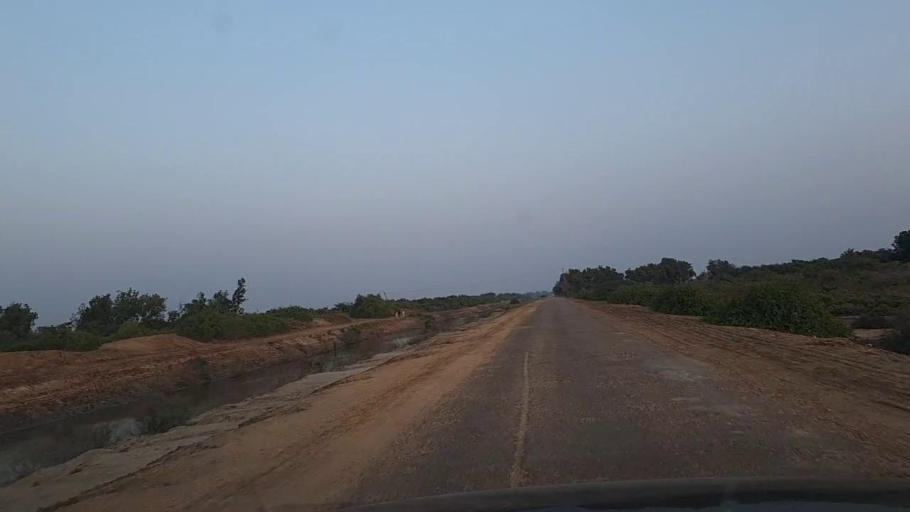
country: PK
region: Sindh
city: Mirpur Sakro
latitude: 24.6321
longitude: 67.6262
